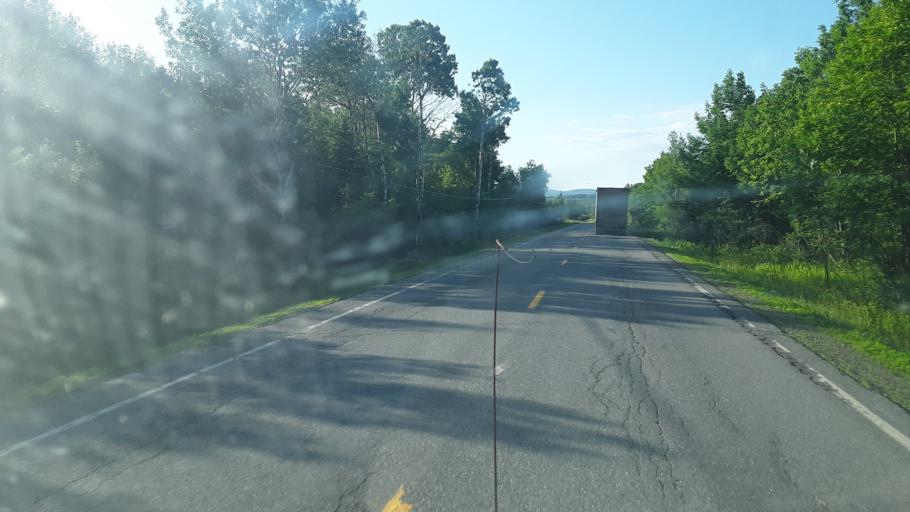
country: US
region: Maine
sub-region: Penobscot County
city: Patten
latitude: 46.1488
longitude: -68.2138
